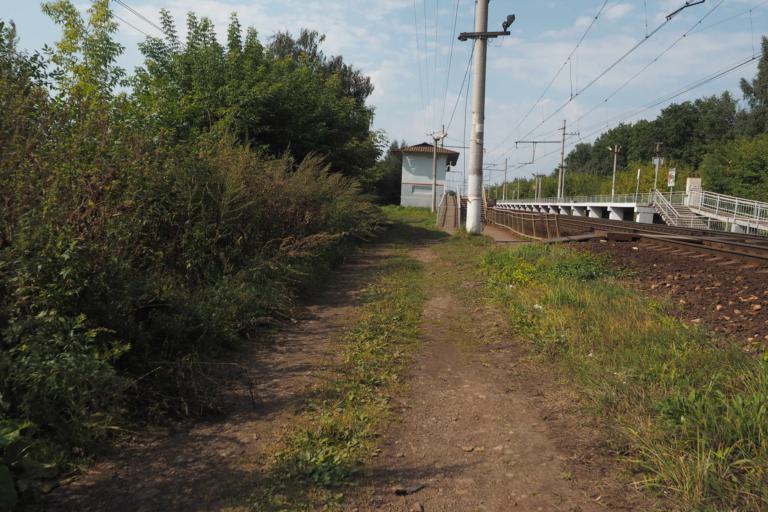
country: RU
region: Moskovskaya
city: Ramenskoye
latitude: 55.5400
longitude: 38.2961
